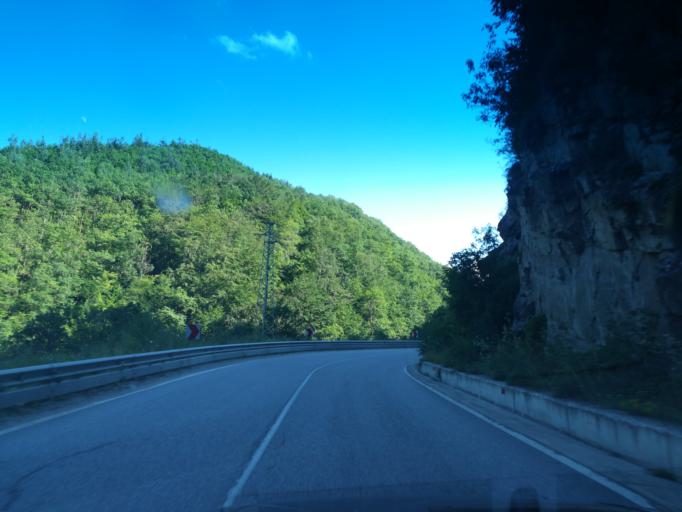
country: BG
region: Smolyan
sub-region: Obshtina Chepelare
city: Chepelare
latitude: 41.7855
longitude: 24.7084
